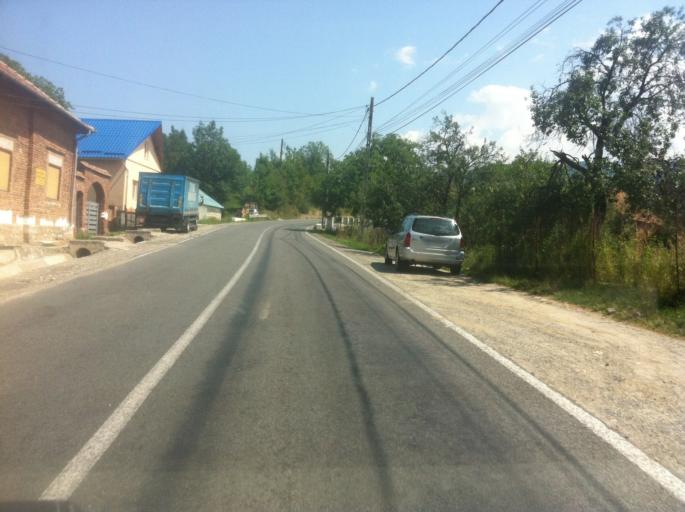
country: RO
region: Caras-Severin
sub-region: Comuna Bautar
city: Bucova
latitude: 45.5088
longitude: 22.6476
